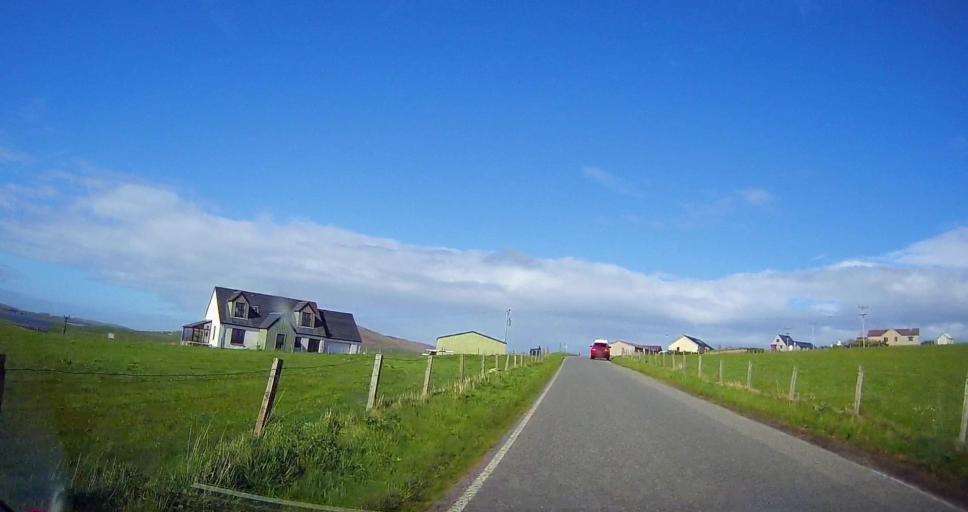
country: GB
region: Scotland
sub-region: Shetland Islands
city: Sandwick
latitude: 59.9152
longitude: -1.3222
